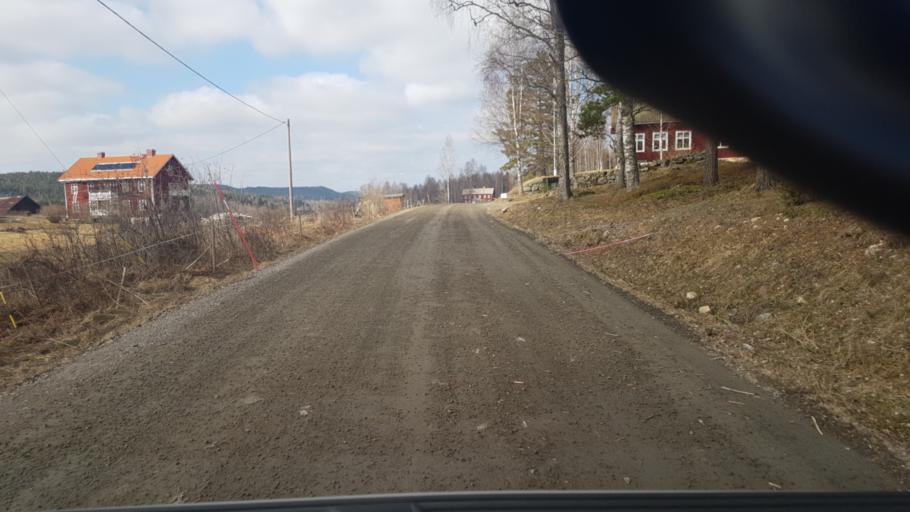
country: SE
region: Vaermland
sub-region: Eda Kommun
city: Amotfors
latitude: 59.7667
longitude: 12.4446
